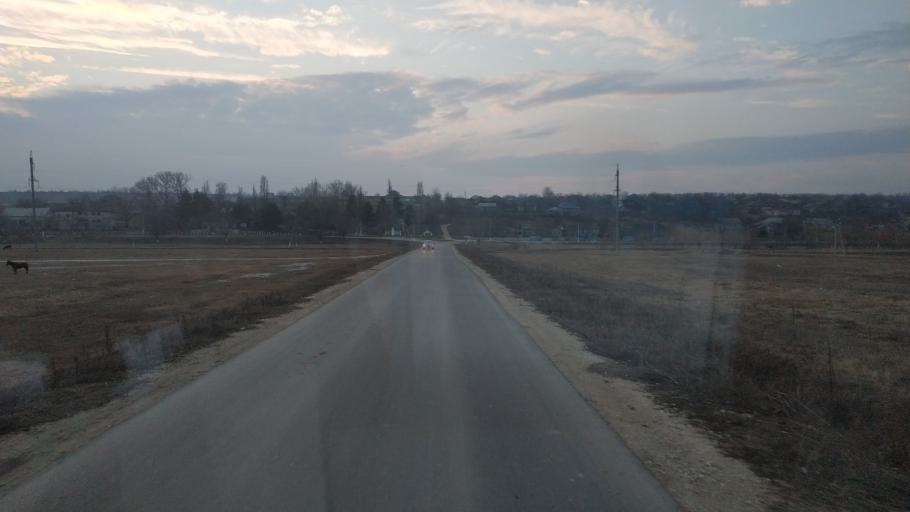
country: MD
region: Hincesti
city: Dancu
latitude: 46.6605
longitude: 28.3098
